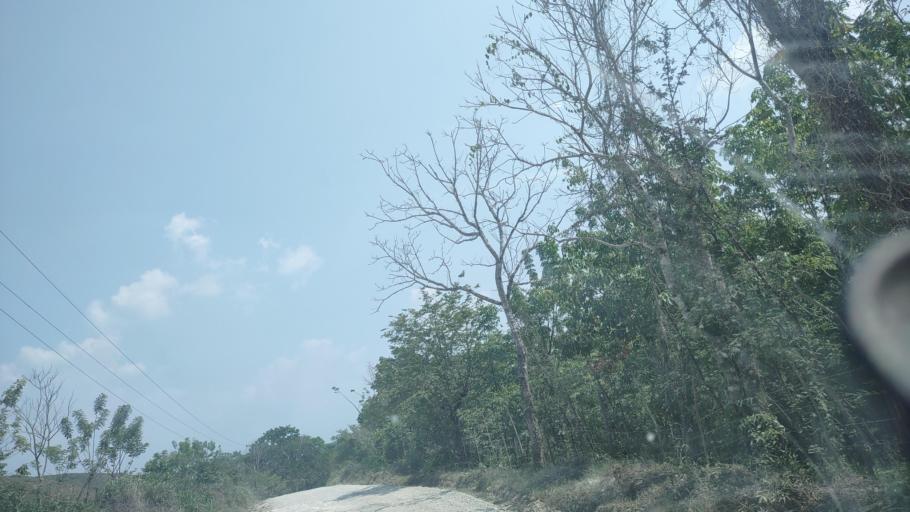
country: MX
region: Tabasco
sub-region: Huimanguillo
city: Francisco Rueda
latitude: 17.5794
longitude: -93.8887
